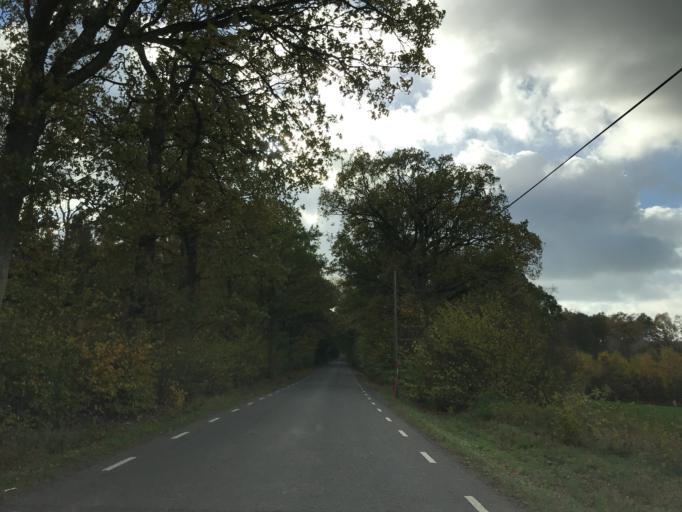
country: SE
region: Skane
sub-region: Bjuvs Kommun
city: Billesholm
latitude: 56.0218
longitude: 13.0026
